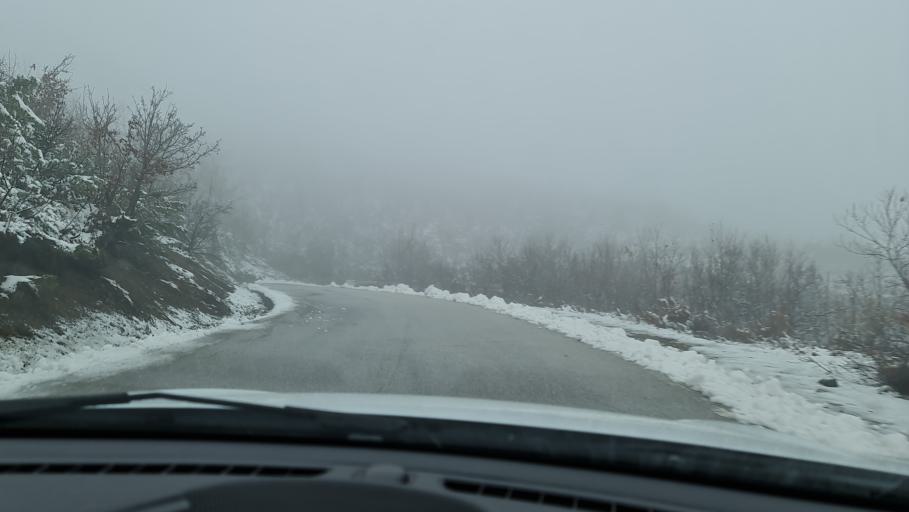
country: AL
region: Kukes
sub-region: Rrethi i Kukesit
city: Kolsh
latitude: 42.0835
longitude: 20.2941
